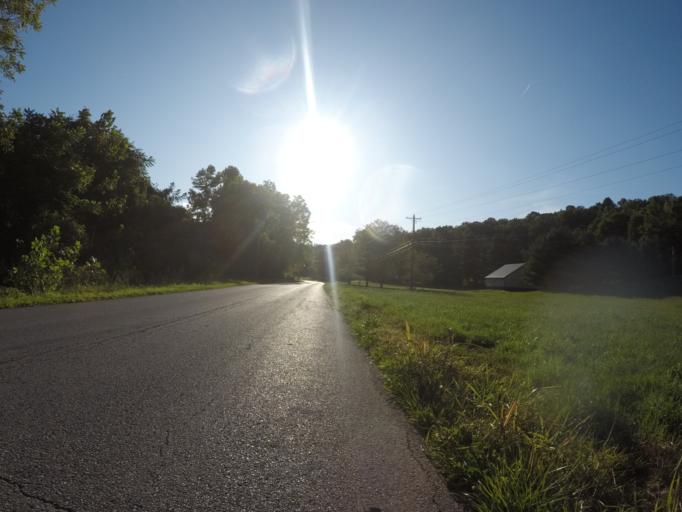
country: US
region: Ohio
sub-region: Lawrence County
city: Coal Grove
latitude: 38.5388
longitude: -82.5362
